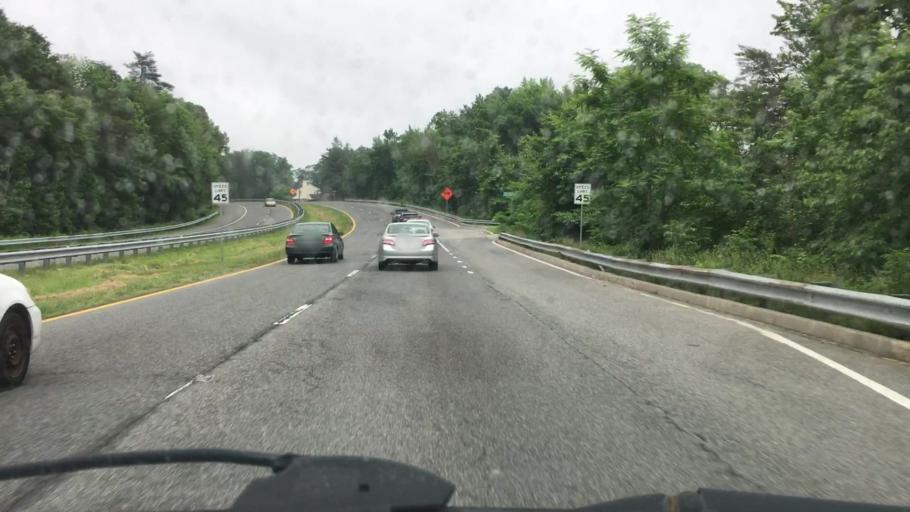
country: US
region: Maryland
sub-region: Prince George's County
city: Goddard
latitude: 38.9907
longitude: -76.8518
